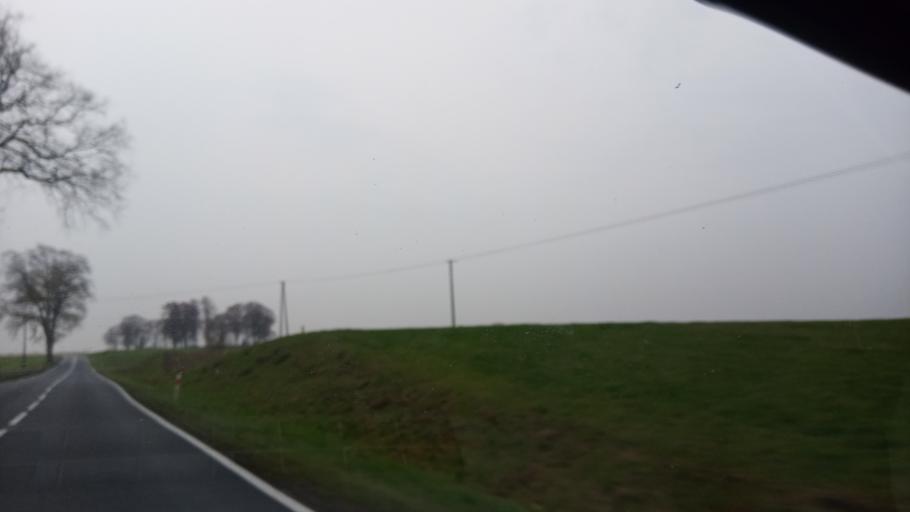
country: PL
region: Kujawsko-Pomorskie
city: Kamien Krajenski
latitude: 53.5556
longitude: 17.5021
